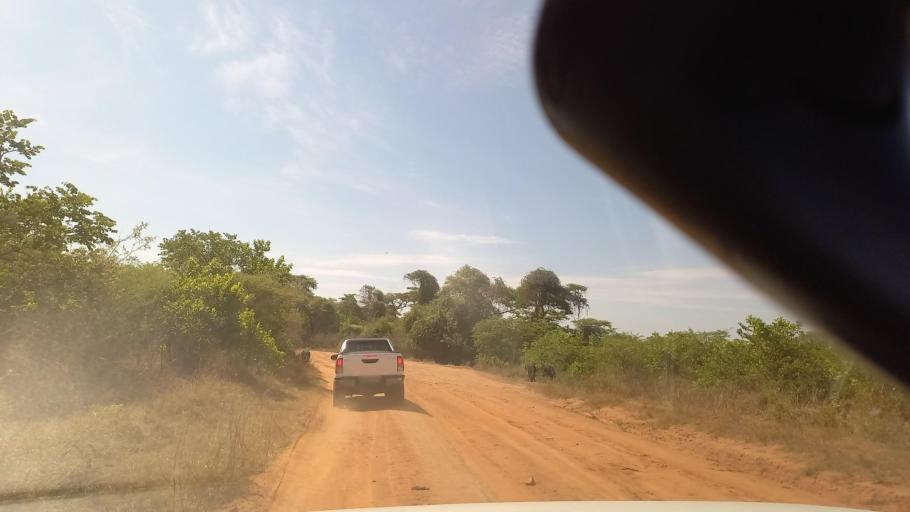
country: ZM
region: Southern
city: Mazabuka
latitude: -16.0394
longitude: 27.6186
